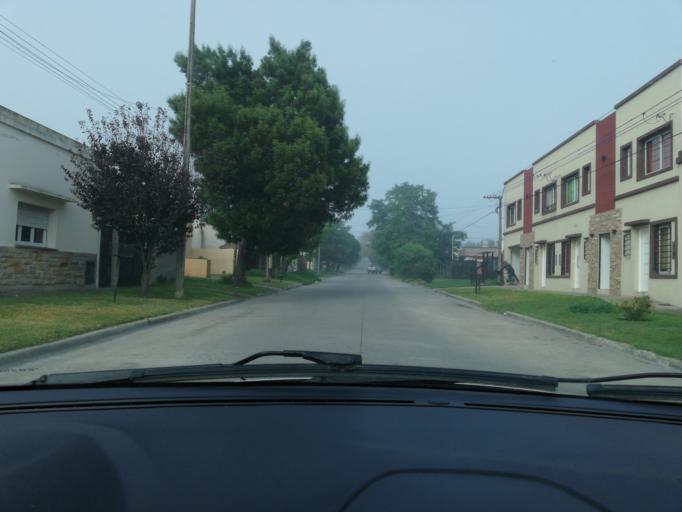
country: AR
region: Buenos Aires
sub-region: Partido de Balcarce
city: Balcarce
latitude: -37.8548
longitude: -58.2469
